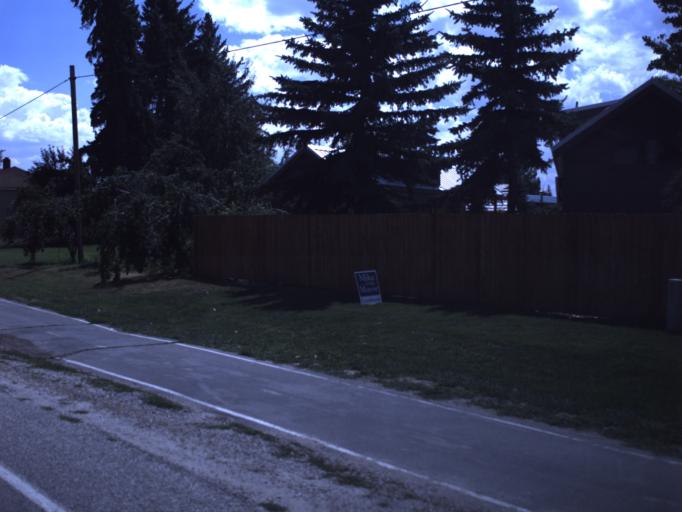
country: US
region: Idaho
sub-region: Bear Lake County
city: Paris
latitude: 41.9552
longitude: -111.3966
